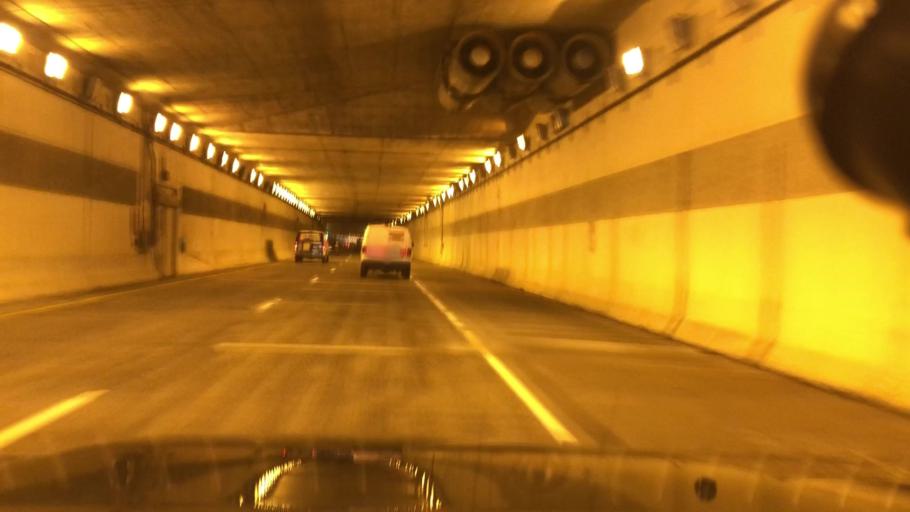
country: US
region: New Jersey
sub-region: Mercer County
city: Trenton
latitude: 40.1958
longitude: -74.7574
